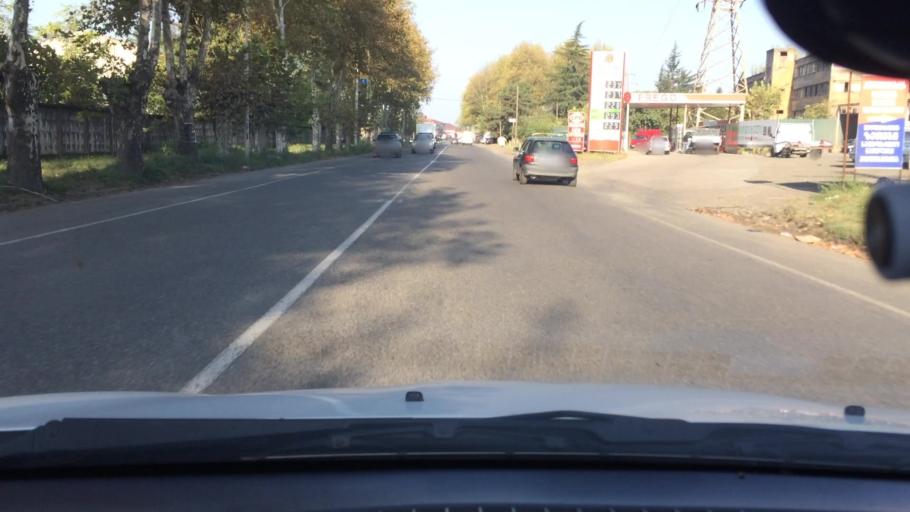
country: GE
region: Imereti
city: Zestap'oni
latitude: 42.1183
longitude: 43.0162
